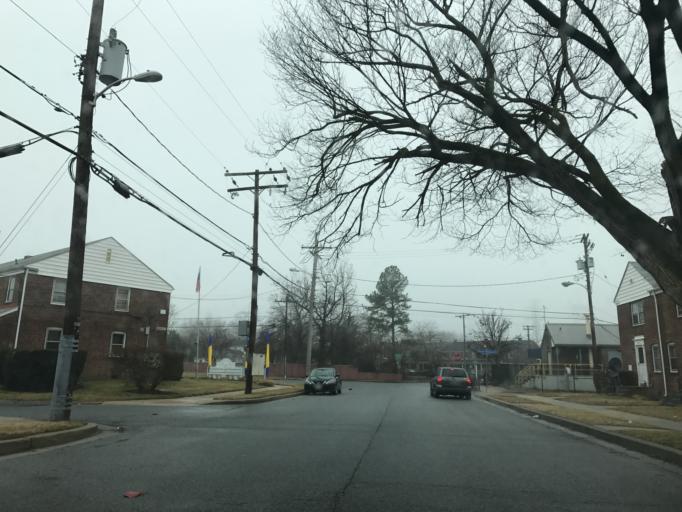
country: US
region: Maryland
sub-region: Baltimore County
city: Dundalk
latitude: 39.2397
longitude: -76.5056
